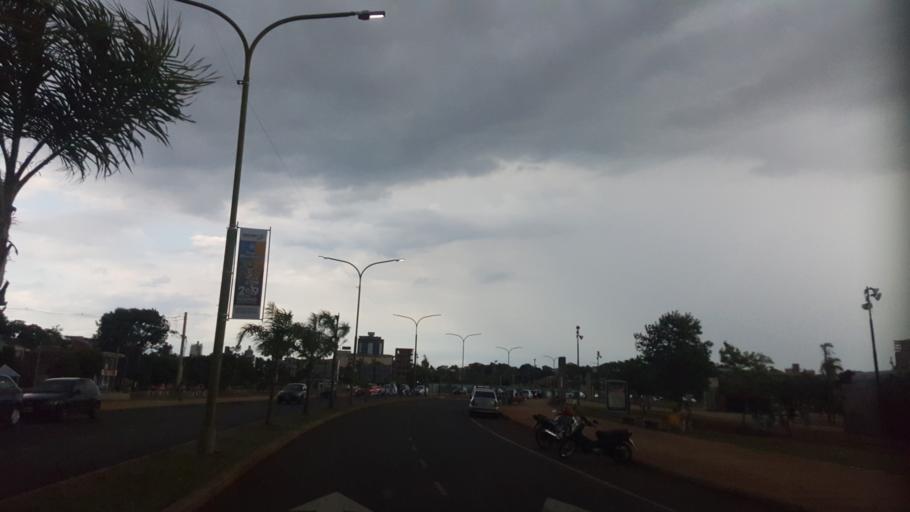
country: AR
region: Misiones
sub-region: Departamento de Capital
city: Posadas
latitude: -27.3545
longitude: -55.9024
